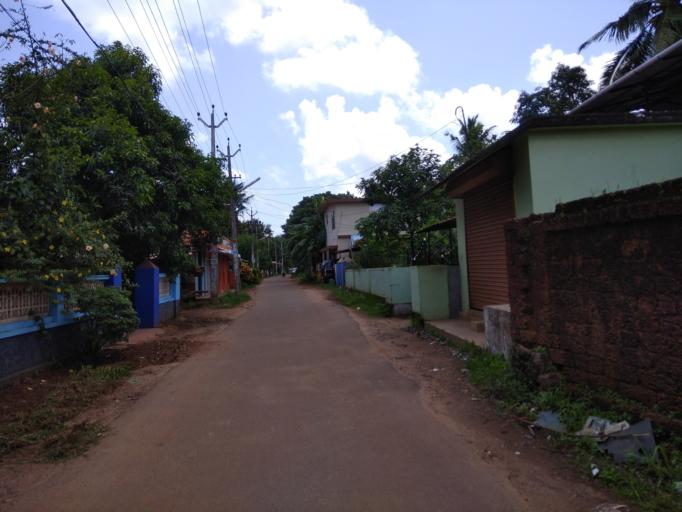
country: IN
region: Kerala
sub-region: Thrissur District
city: Avanoor
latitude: 10.5638
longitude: 76.1724
